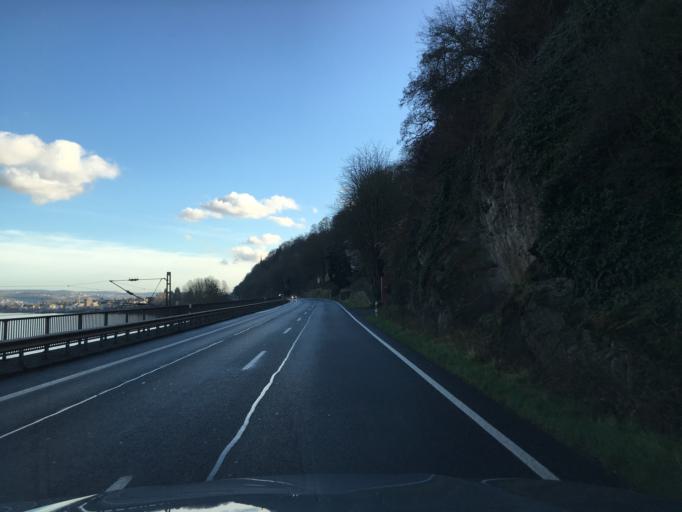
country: DE
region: Rheinland-Pfalz
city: Unkel
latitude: 50.5873
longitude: 7.2128
